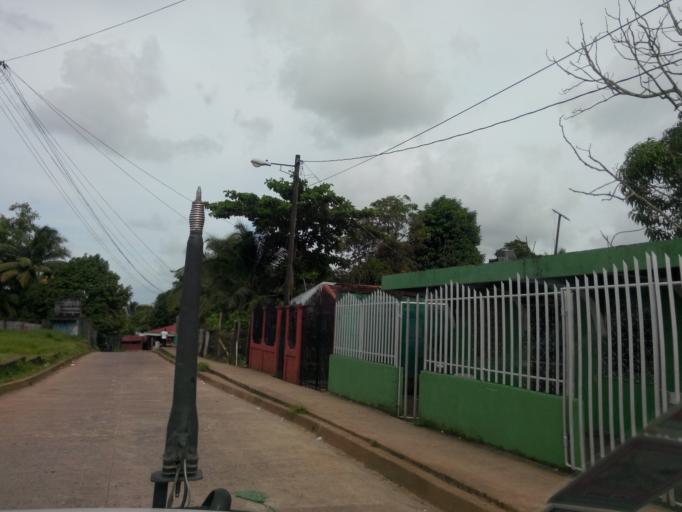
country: NI
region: Atlantico Sur
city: Bluefields
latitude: 12.0239
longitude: -83.7628
